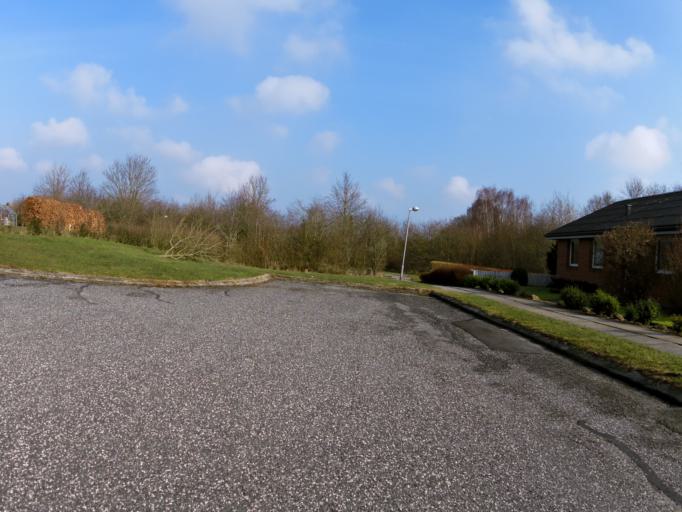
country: DK
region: Central Jutland
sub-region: Arhus Kommune
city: Marslet
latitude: 56.0849
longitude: 10.1482
